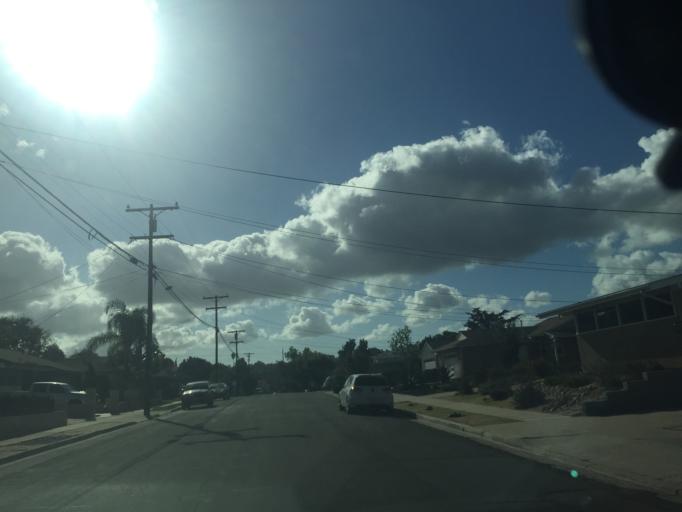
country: US
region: California
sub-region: San Diego County
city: La Mesa
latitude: 32.7901
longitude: -117.0929
